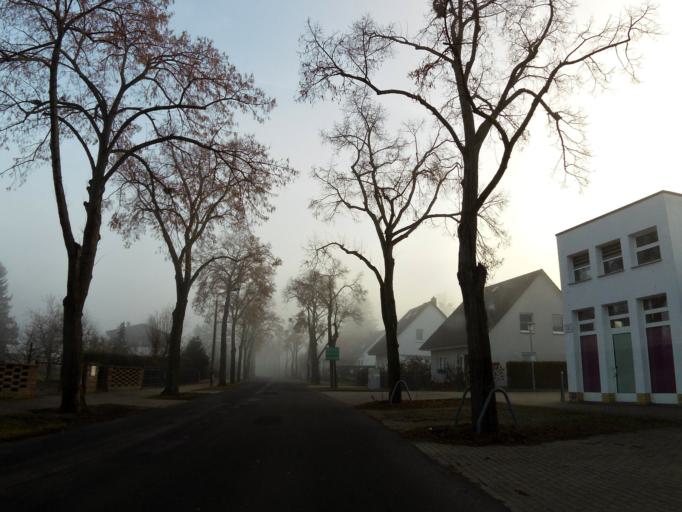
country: DE
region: Brandenburg
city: Werder
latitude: 52.3613
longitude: 12.9747
